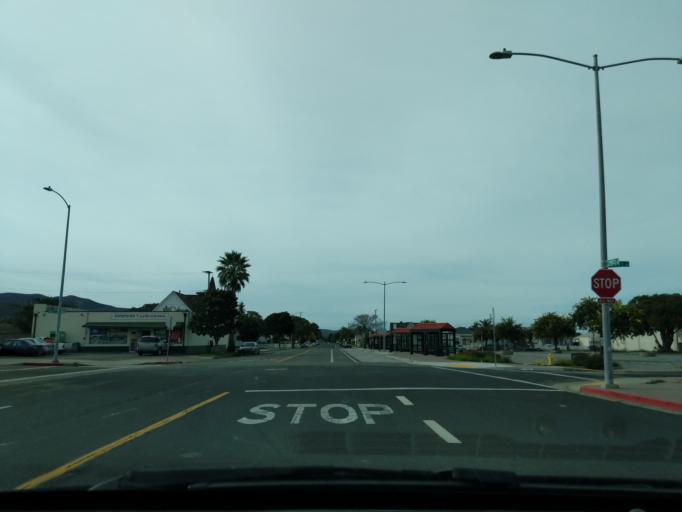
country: US
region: California
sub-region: Santa Barbara County
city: Lompoc
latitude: 34.6373
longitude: -120.4590
